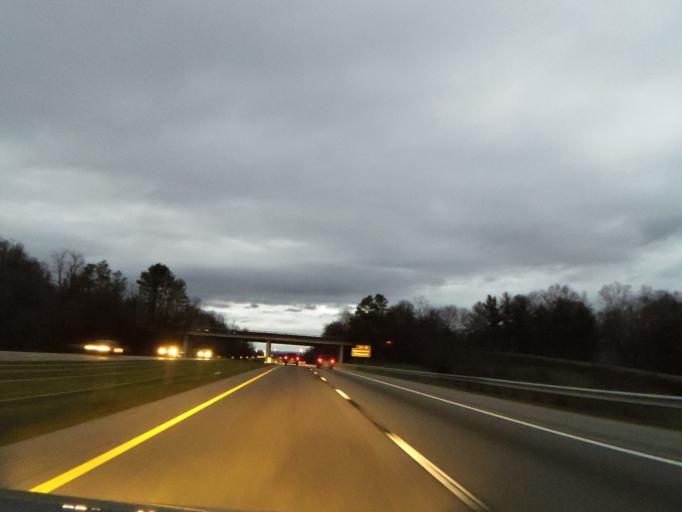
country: US
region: Tennessee
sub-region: Washington County
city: Gray
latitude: 36.3988
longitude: -82.4624
